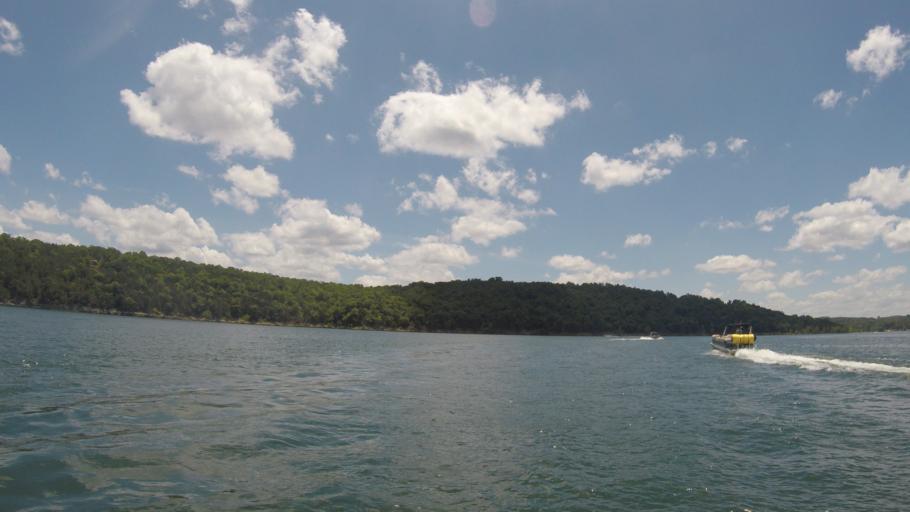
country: US
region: Missouri
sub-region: Barry County
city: Shell Knob
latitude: 36.5940
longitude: -93.5402
